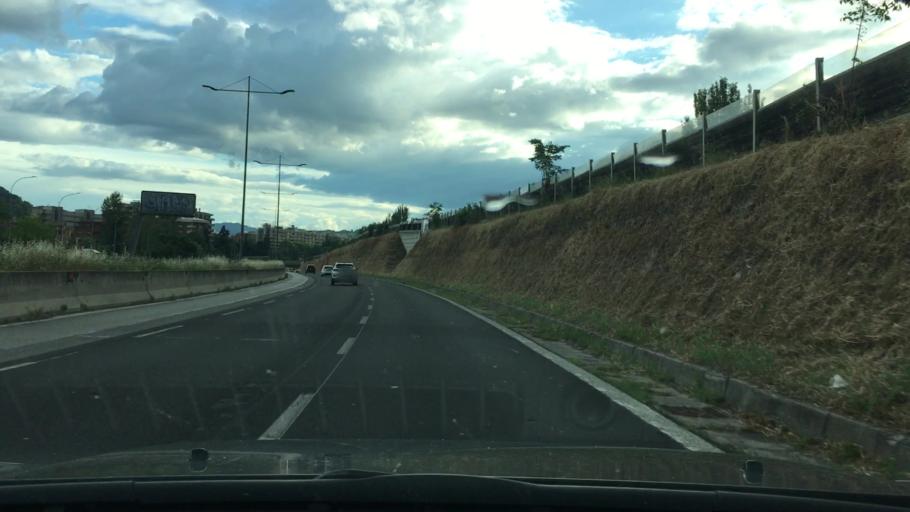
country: IT
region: Emilia-Romagna
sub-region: Provincia di Bologna
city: Casalecchio di Reno
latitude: 44.4977
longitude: 11.2993
